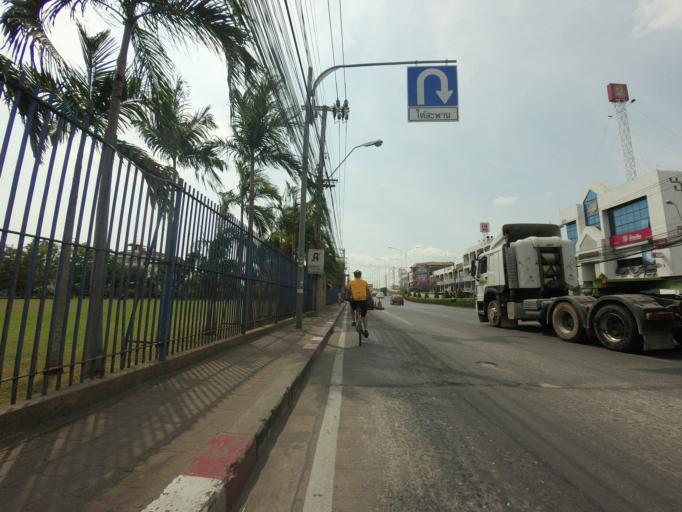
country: TH
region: Bangkok
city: Lat Krabang
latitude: 13.7217
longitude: 100.7813
